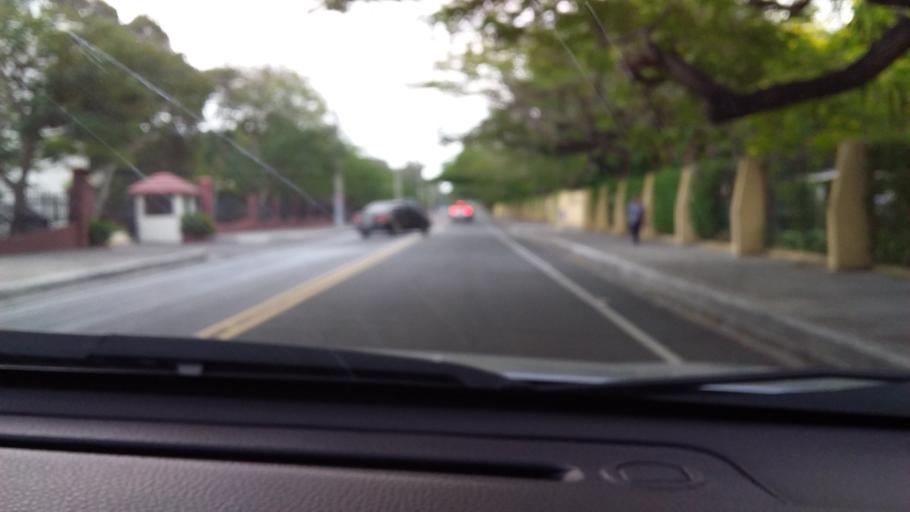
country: DO
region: Nacional
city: Bella Vista
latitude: 18.4556
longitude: -69.9366
